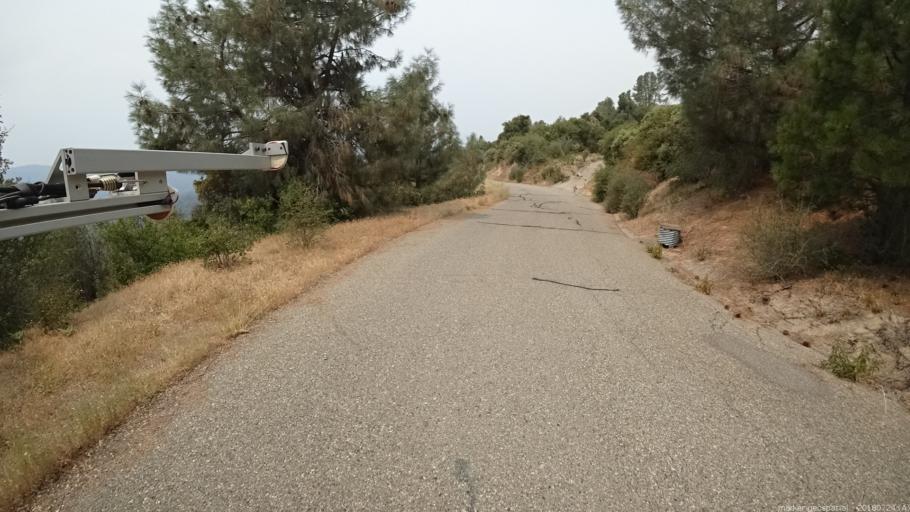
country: US
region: California
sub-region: Madera County
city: Oakhurst
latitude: 37.3212
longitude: -119.5947
